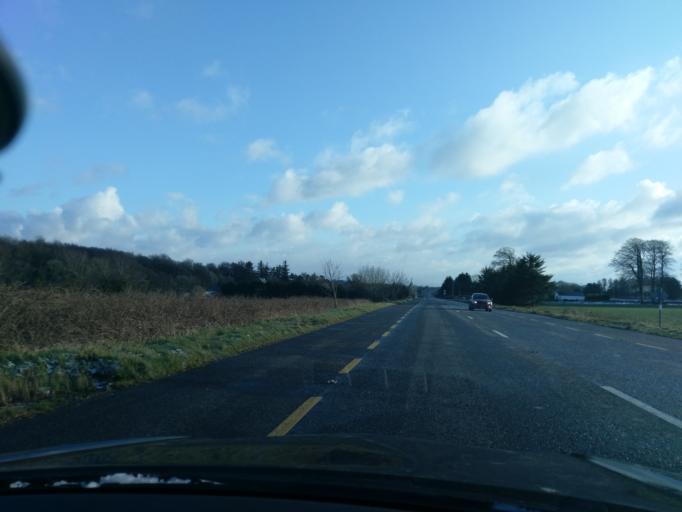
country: IE
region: Connaught
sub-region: County Galway
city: Gort
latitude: 53.1510
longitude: -8.8057
